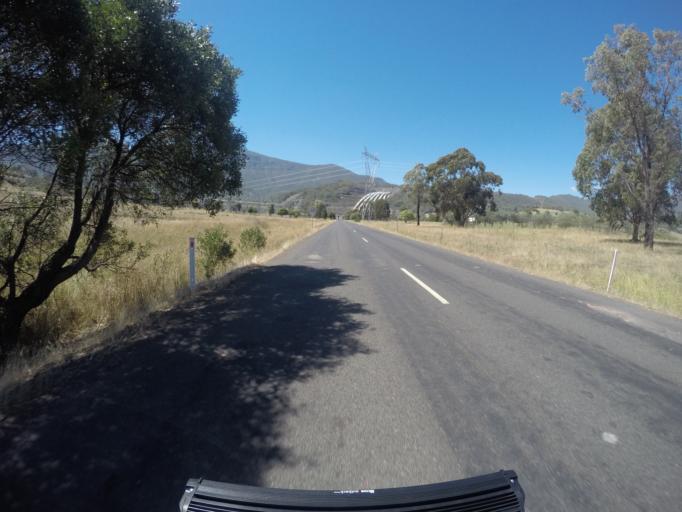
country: AU
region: New South Wales
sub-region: Tumut Shire
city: Tumut
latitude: -35.6060
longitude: 148.2847
